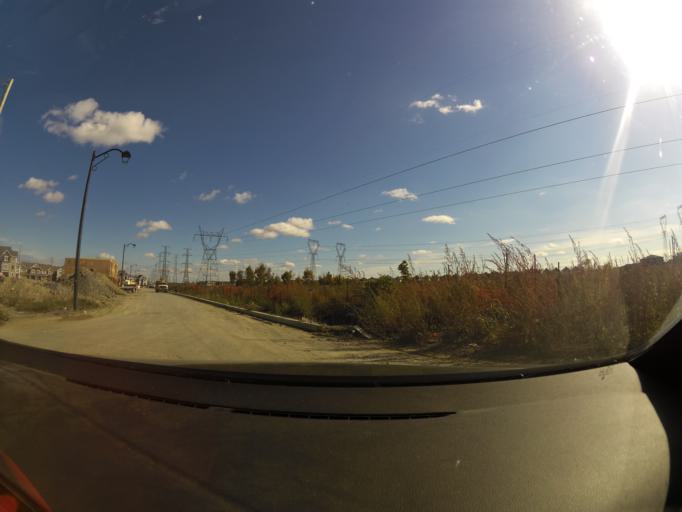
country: CA
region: Ontario
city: Bells Corners
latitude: 45.2801
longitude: -75.8896
